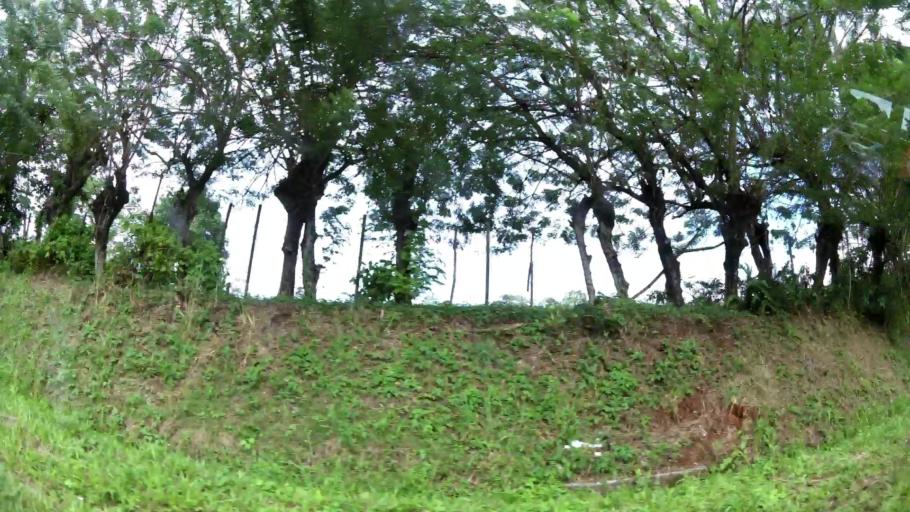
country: MQ
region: Martinique
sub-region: Martinique
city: Saint-Joseph
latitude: 14.6522
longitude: -61.0407
